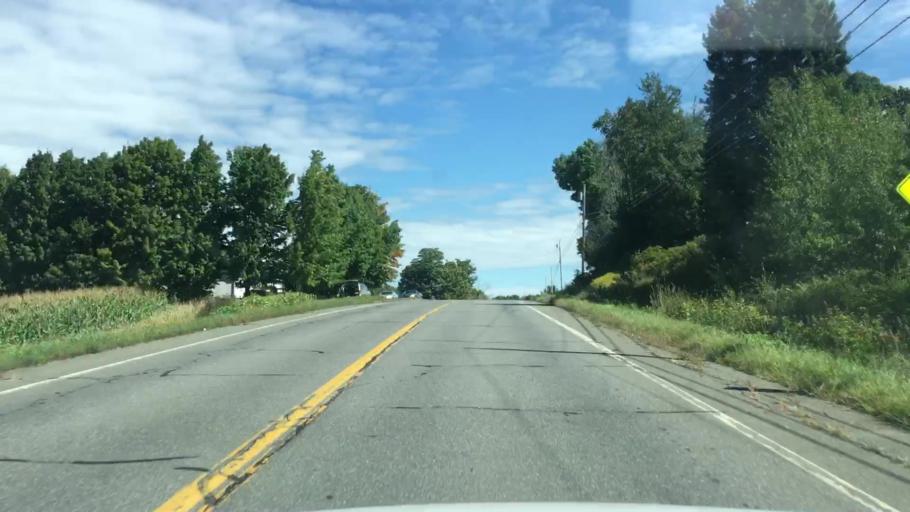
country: US
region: Maine
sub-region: Penobscot County
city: Dexter
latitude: 45.0738
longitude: -69.2347
